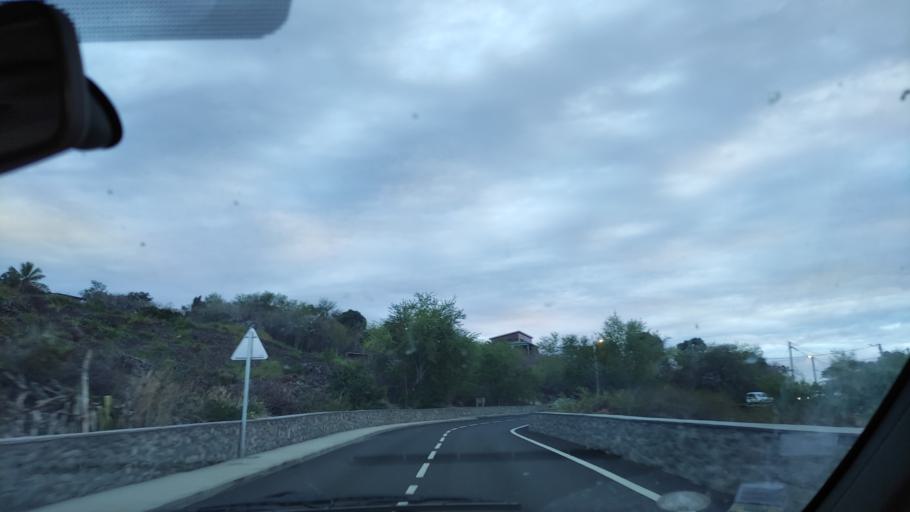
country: RE
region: Reunion
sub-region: Reunion
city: Saint-Leu
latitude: -21.1937
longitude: 55.2914
